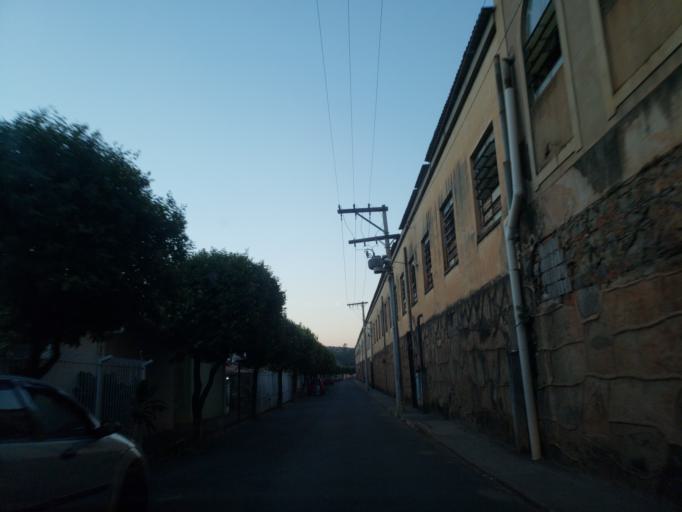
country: BR
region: Minas Gerais
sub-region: Sao Joao Nepomuceno
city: Sao Joao Nepomuceno
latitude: -21.5327
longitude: -43.0148
